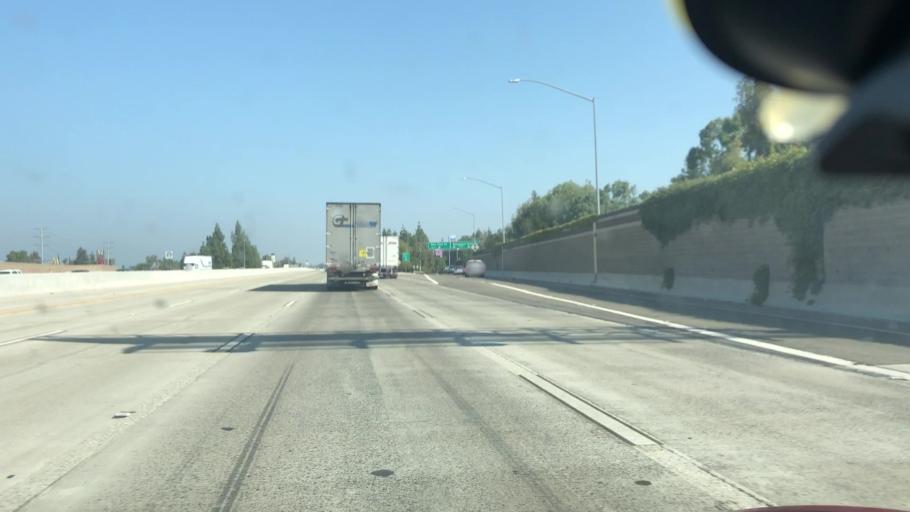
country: US
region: California
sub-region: San Joaquin County
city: Lincoln Village
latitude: 38.0015
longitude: -121.3500
